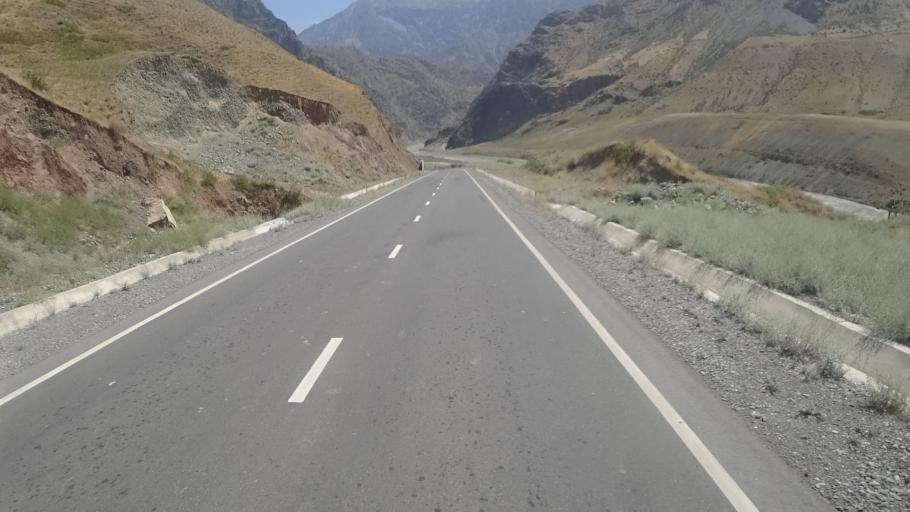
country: AF
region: Badakhshan
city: Deh Khwahan
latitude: 37.9401
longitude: 70.2261
